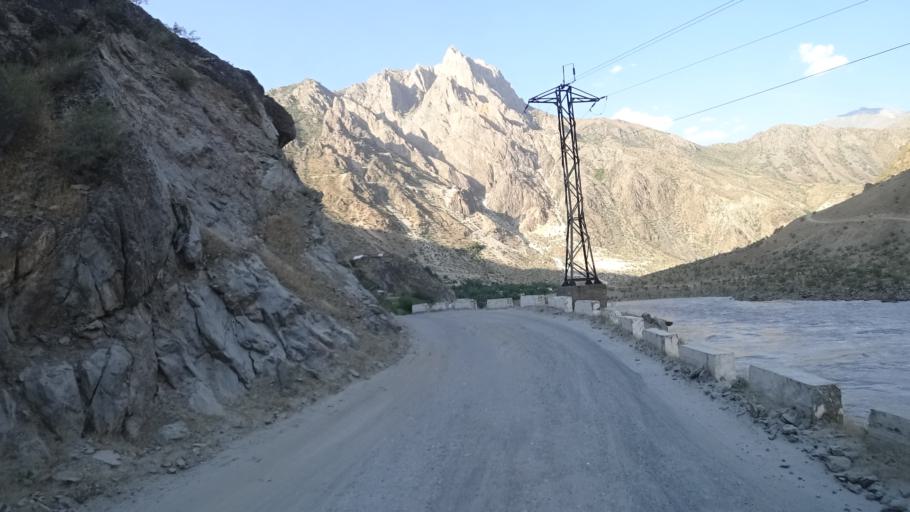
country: AF
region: Badakhshan
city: Maymay
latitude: 38.4883
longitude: 70.9842
